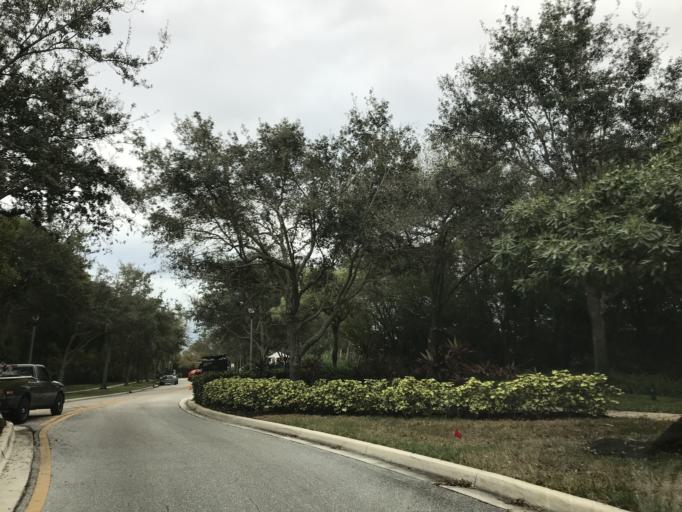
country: US
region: Florida
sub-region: Palm Beach County
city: Jupiter
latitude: 26.9162
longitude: -80.1006
